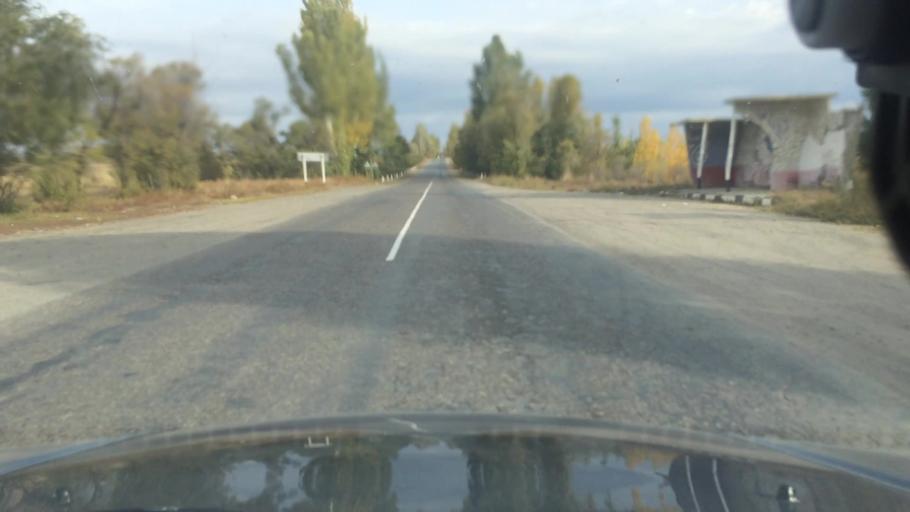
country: KG
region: Ysyk-Koel
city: Karakol
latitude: 42.5649
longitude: 78.3913
